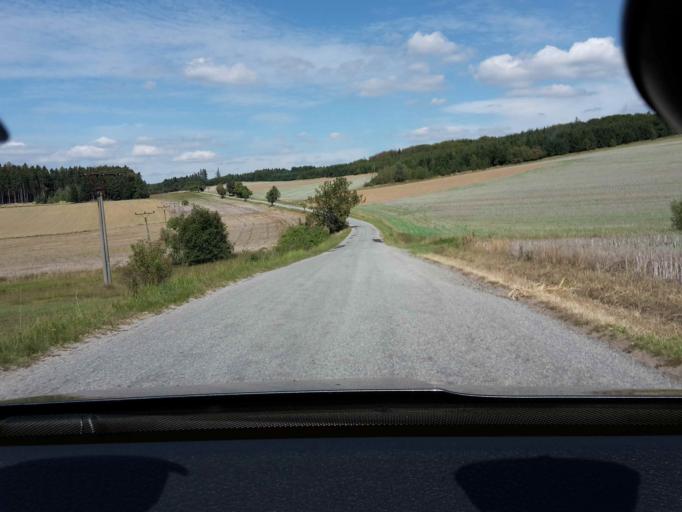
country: CZ
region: Vysocina
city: Zeletava
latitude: 49.1220
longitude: 15.6095
